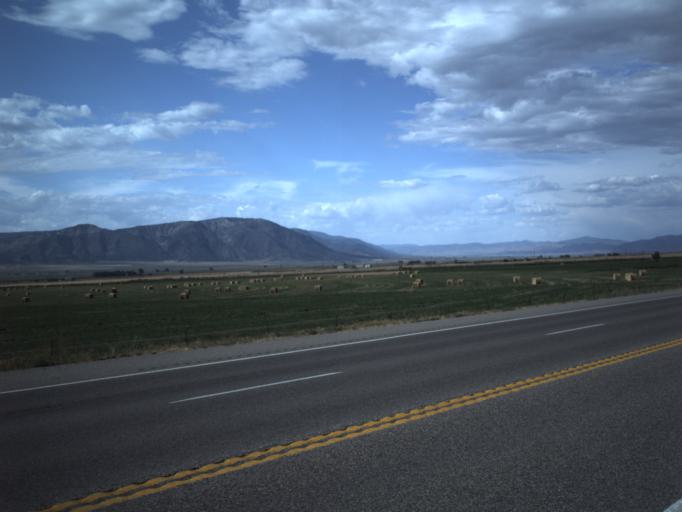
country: US
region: Utah
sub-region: Sanpete County
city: Manti
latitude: 39.3124
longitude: -111.6110
